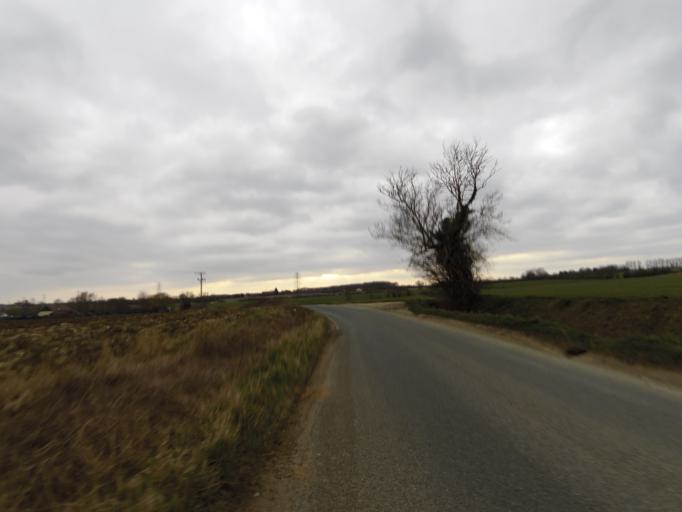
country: GB
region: England
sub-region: Suffolk
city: Ipswich
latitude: 52.1312
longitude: 1.1550
